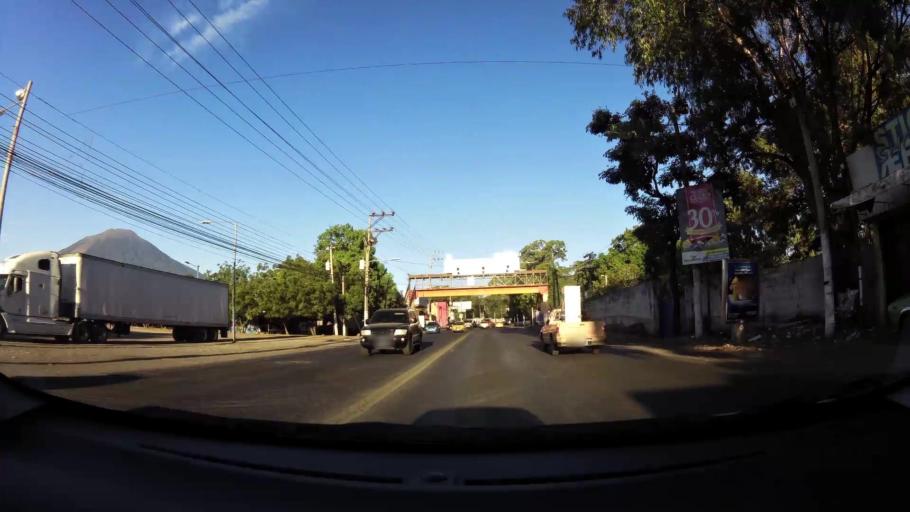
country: SV
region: San Miguel
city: San Miguel
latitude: 13.4694
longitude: -88.1806
